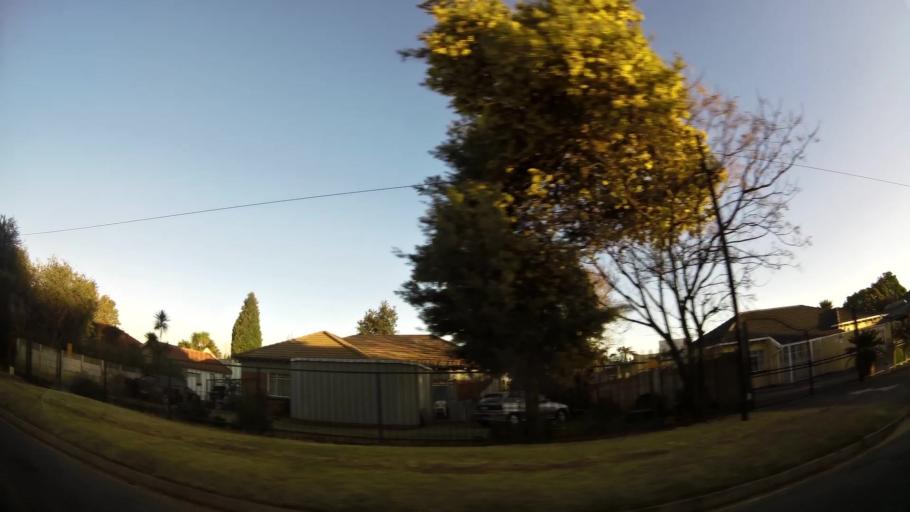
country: ZA
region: Gauteng
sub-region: City of Johannesburg Metropolitan Municipality
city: Roodepoort
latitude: -26.1502
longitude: 27.8834
